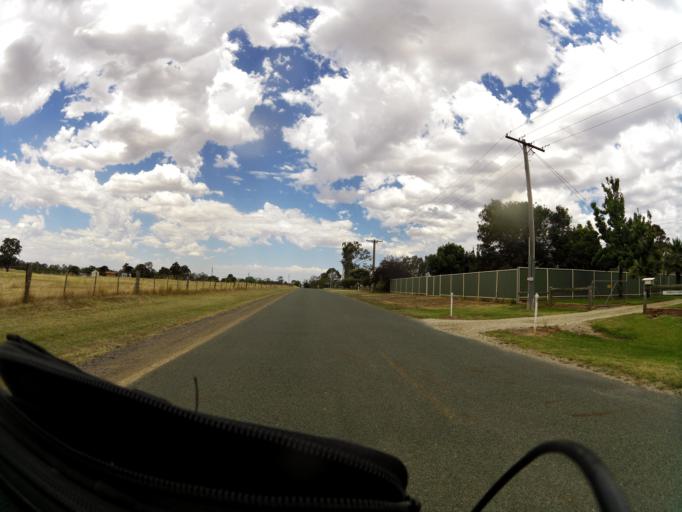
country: AU
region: Victoria
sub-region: Campaspe
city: Kyabram
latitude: -36.7427
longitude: 145.1360
